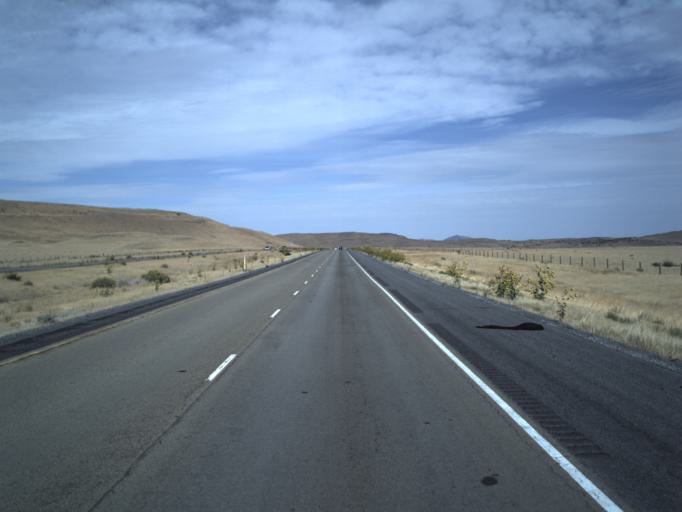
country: US
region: Utah
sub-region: Tooele County
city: Grantsville
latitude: 40.8054
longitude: -112.8588
